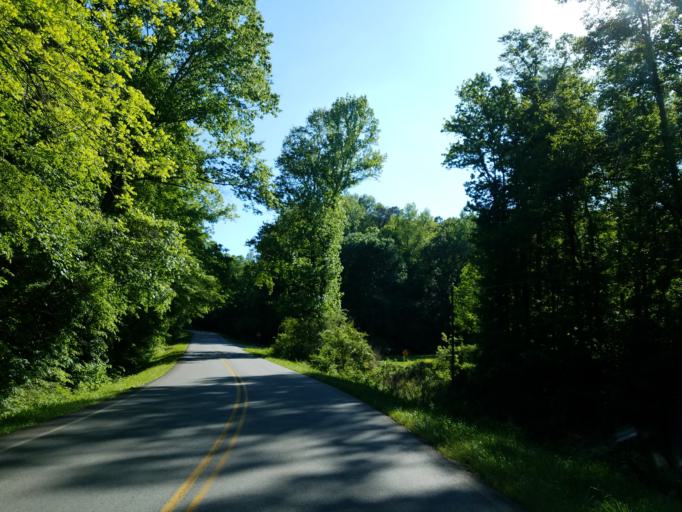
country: US
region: Georgia
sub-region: Pickens County
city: Jasper
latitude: 34.5668
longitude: -84.5162
